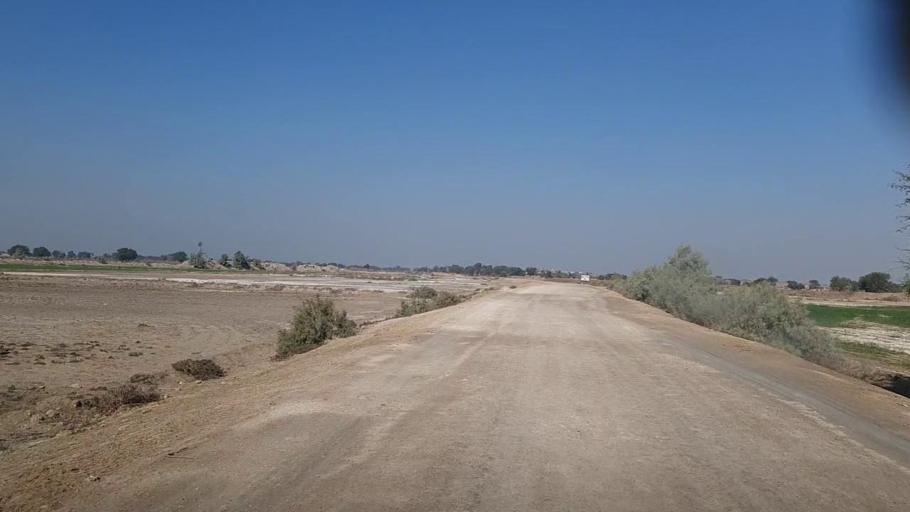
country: PK
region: Sindh
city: Khairpur
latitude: 27.9807
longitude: 69.8495
